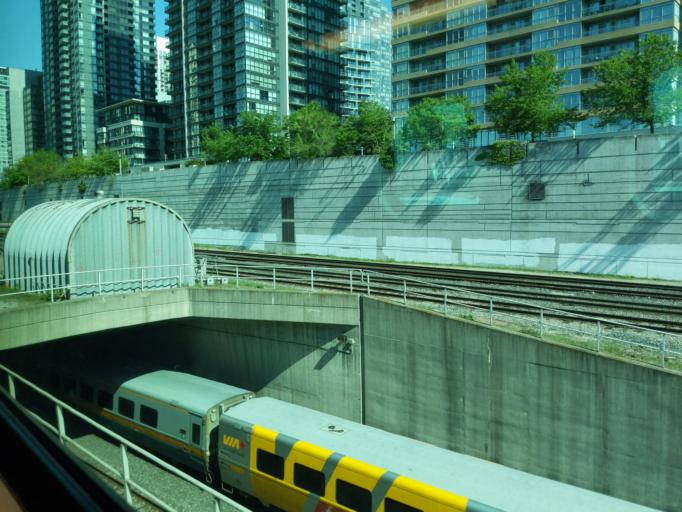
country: CA
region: Ontario
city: Toronto
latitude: 43.6411
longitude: -79.3971
